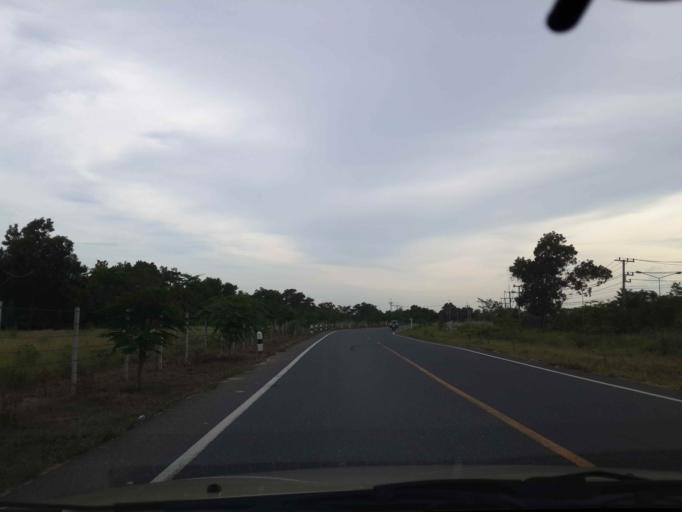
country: TH
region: Chon Buri
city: Phatthaya
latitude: 12.9172
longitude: 101.0009
